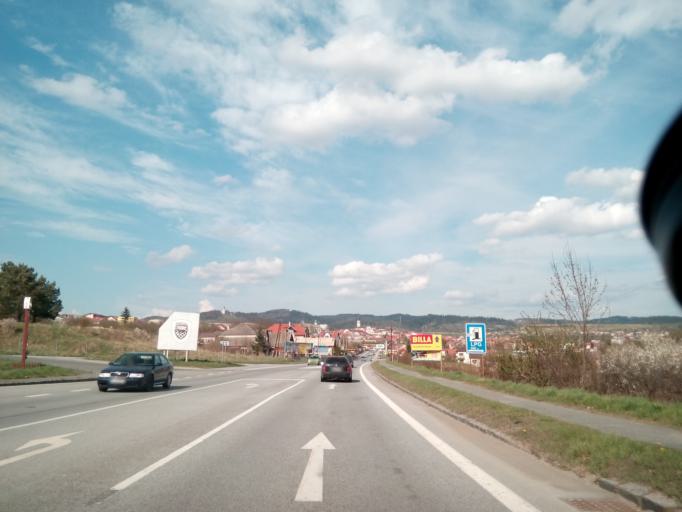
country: SK
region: Presovsky
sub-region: Okres Presov
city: Levoca
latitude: 49.0150
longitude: 20.5729
